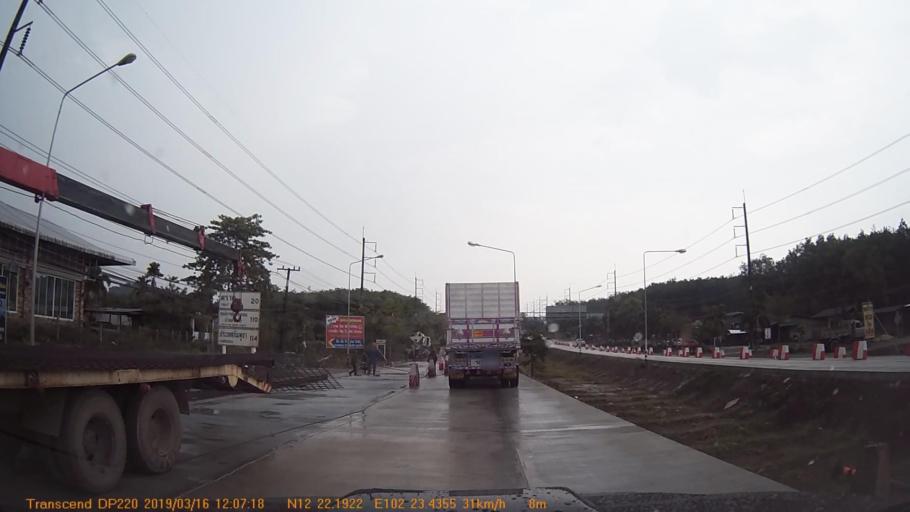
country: TH
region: Trat
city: Khao Saming
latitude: 12.3661
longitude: 102.3978
